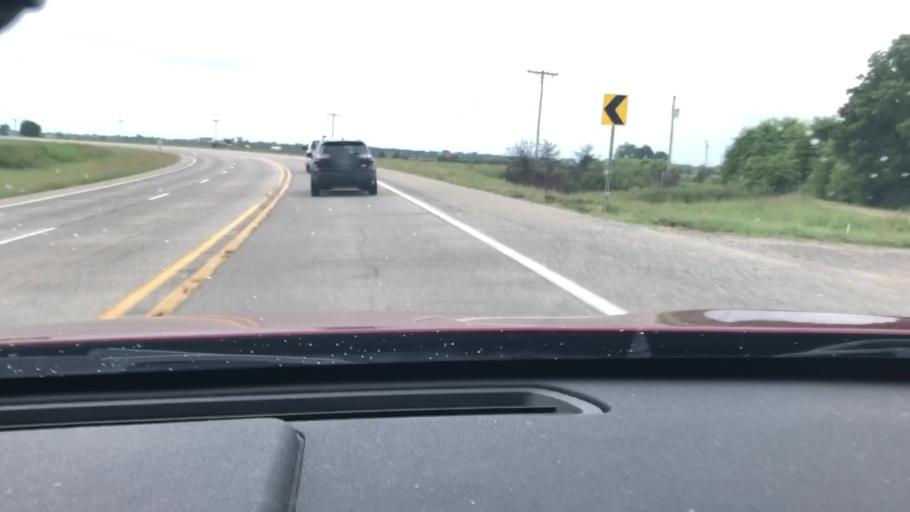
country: US
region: Arkansas
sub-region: Lafayette County
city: Lewisville
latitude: 33.3974
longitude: -93.7445
